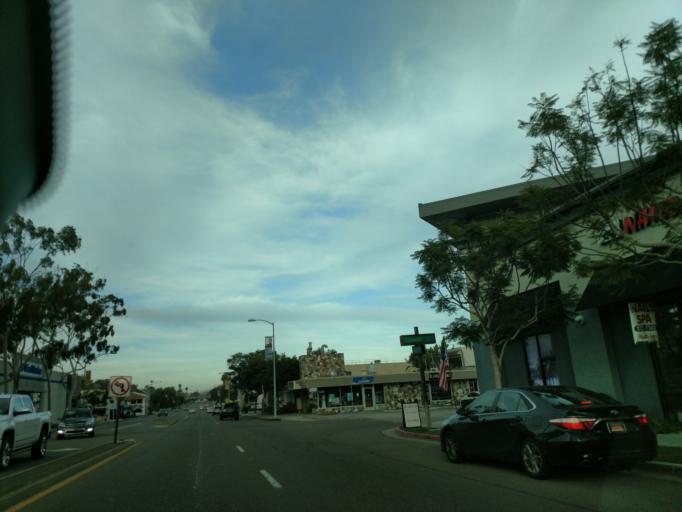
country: US
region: California
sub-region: San Diego County
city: Coronado
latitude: 32.7229
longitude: -117.2307
